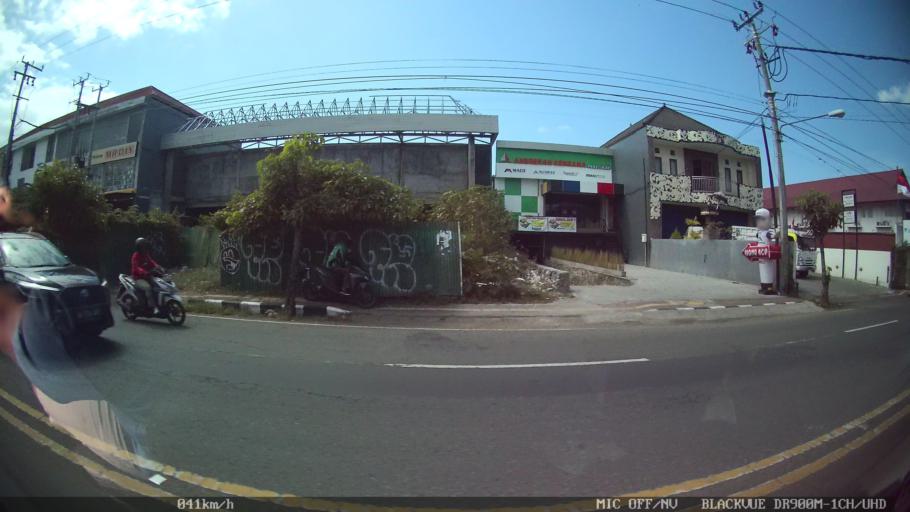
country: ID
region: Bali
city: Karyadharma
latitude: -8.6825
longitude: 115.1891
